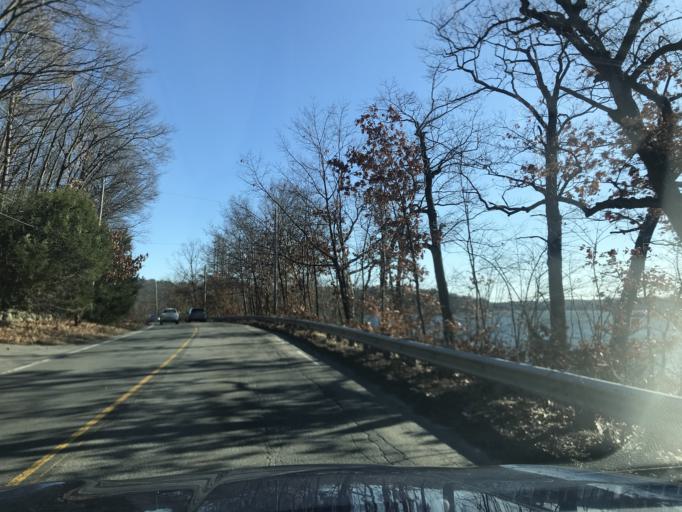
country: US
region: Massachusetts
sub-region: Essex County
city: North Andover
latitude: 42.7143
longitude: -71.1052
